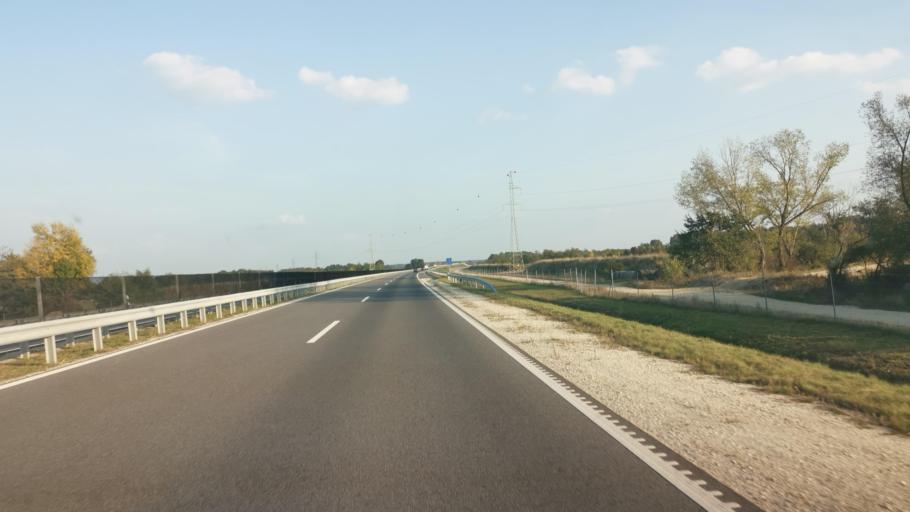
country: HU
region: Gyor-Moson-Sopron
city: Kapuvar
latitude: 47.5800
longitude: 16.9868
